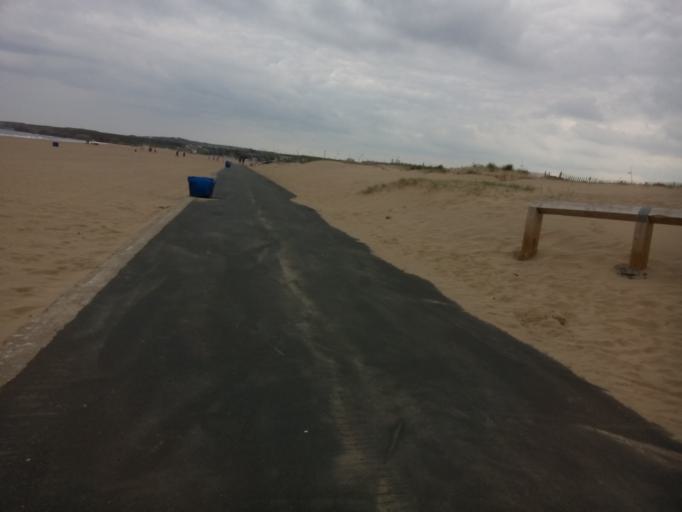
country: GB
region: England
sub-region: South Tyneside
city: South Shields
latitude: 54.9999
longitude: -1.4126
